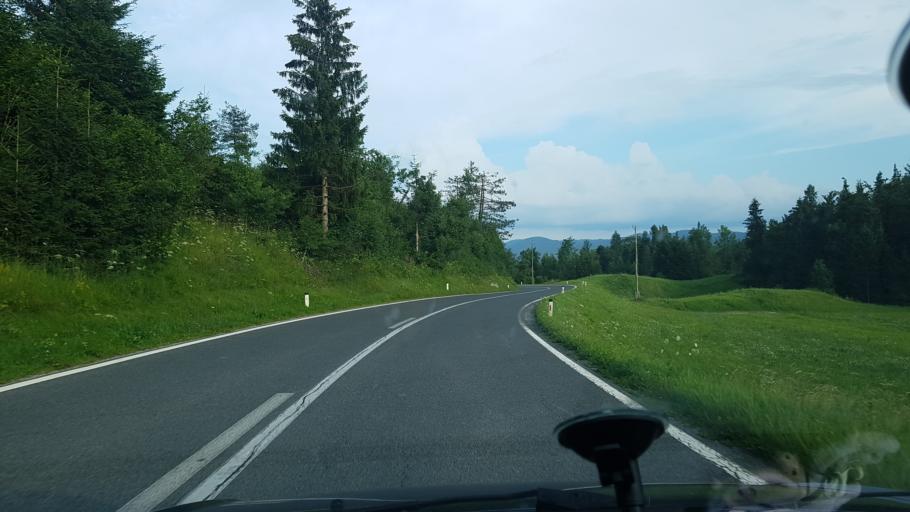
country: SI
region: Ziri
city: Ziri
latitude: 45.9437
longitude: 14.1185
